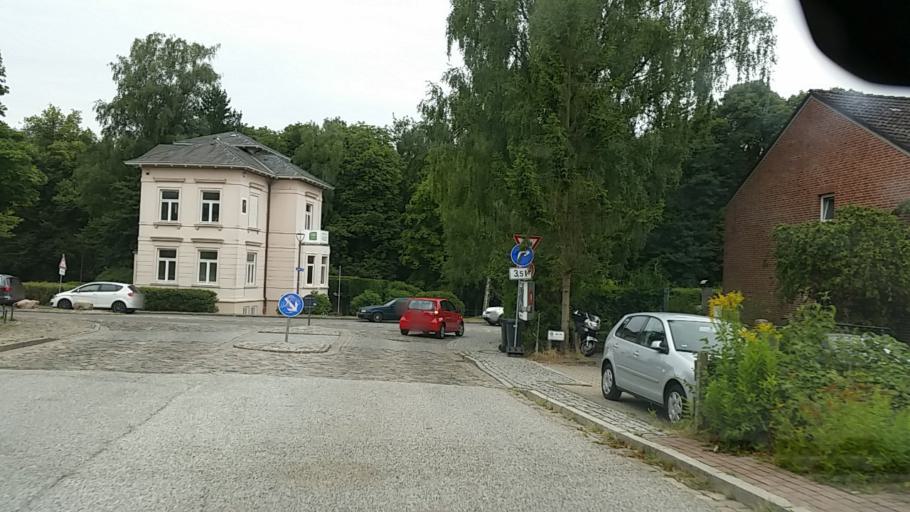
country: DE
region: Schleswig-Holstein
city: Wentorf bei Hamburg
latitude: 53.5076
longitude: 10.2525
